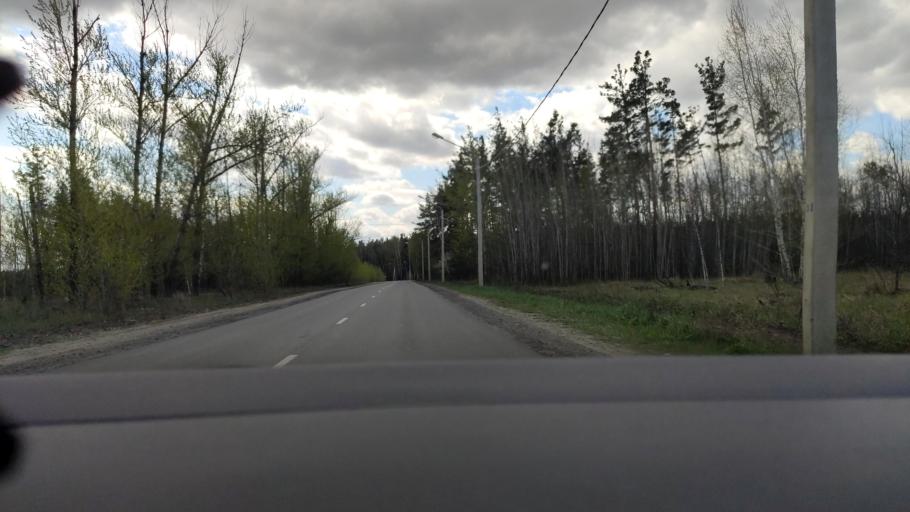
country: RU
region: Voronezj
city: Somovo
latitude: 51.7283
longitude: 39.3188
